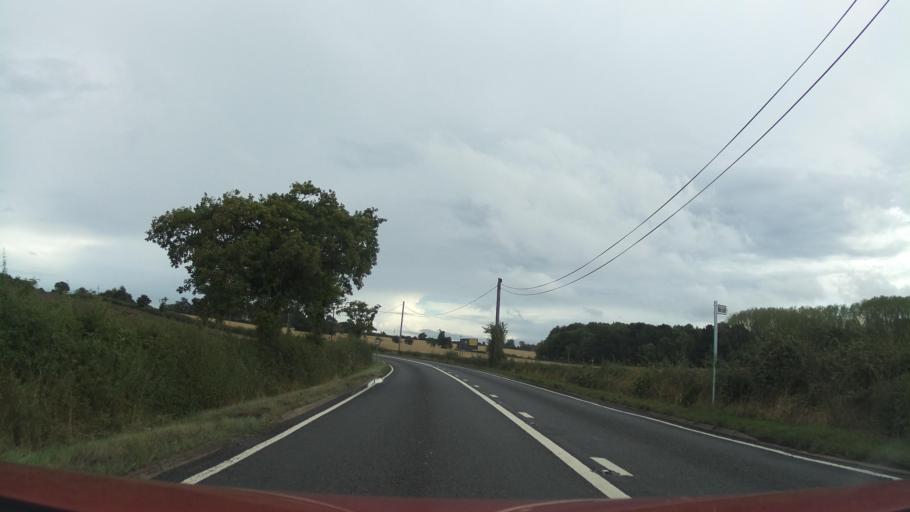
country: GB
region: England
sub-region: Worcestershire
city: Droitwich
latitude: 52.2980
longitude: -2.1752
